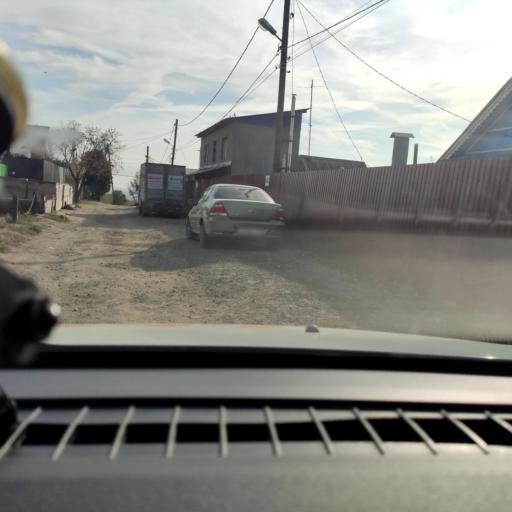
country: RU
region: Samara
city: Samara
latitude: 53.1825
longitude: 50.1797
